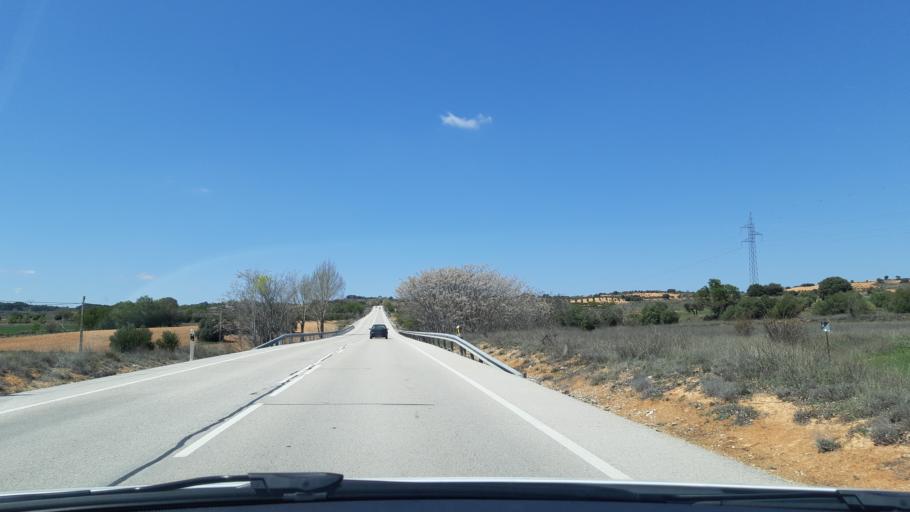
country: ES
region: Castille-La Mancha
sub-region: Provincia de Guadalajara
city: Cifuentes
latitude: 40.7921
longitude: -2.6424
